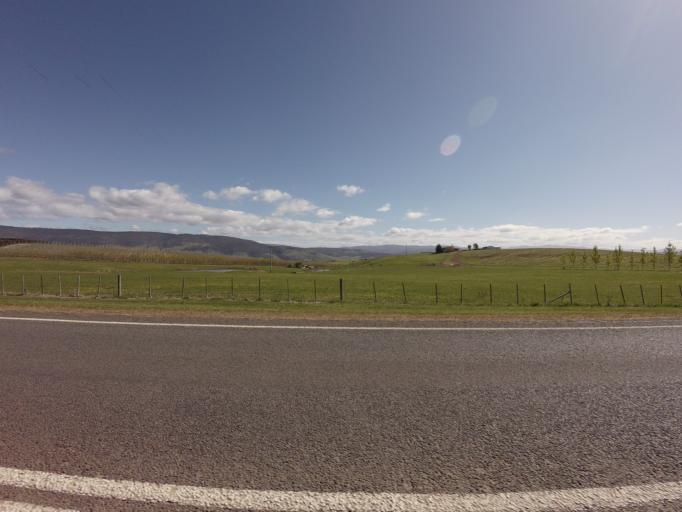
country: AU
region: Tasmania
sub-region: Derwent Valley
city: New Norfolk
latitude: -42.7060
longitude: 146.9441
